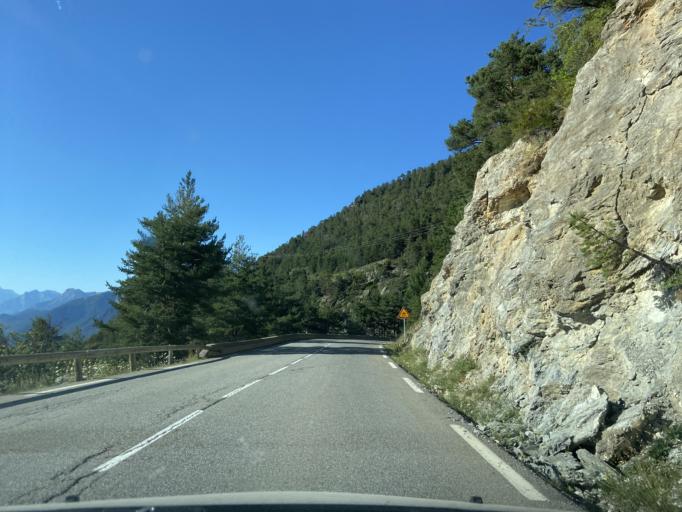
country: FR
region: Provence-Alpes-Cote d'Azur
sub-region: Departement des Hautes-Alpes
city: Guillestre
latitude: 44.6266
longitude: 6.6801
